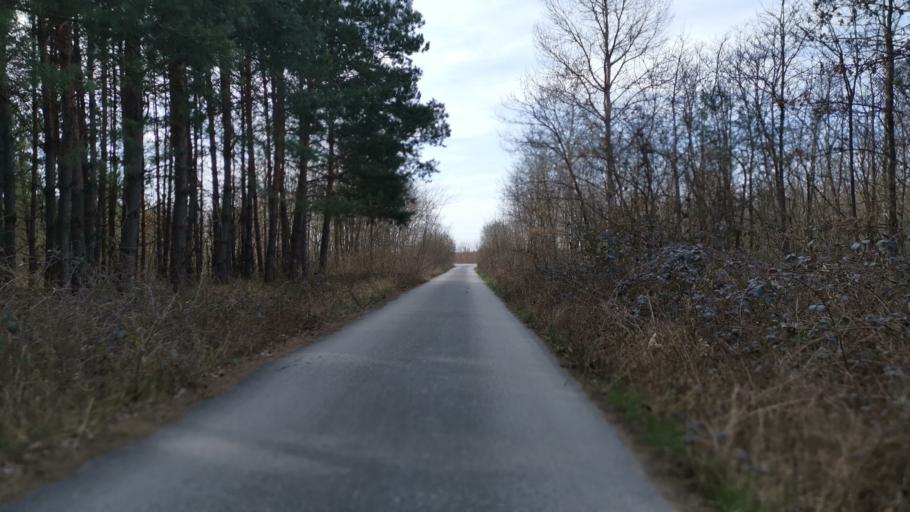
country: CZ
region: South Moravian
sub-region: Okres Breclav
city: Lanzhot
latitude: 48.6931
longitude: 17.0388
